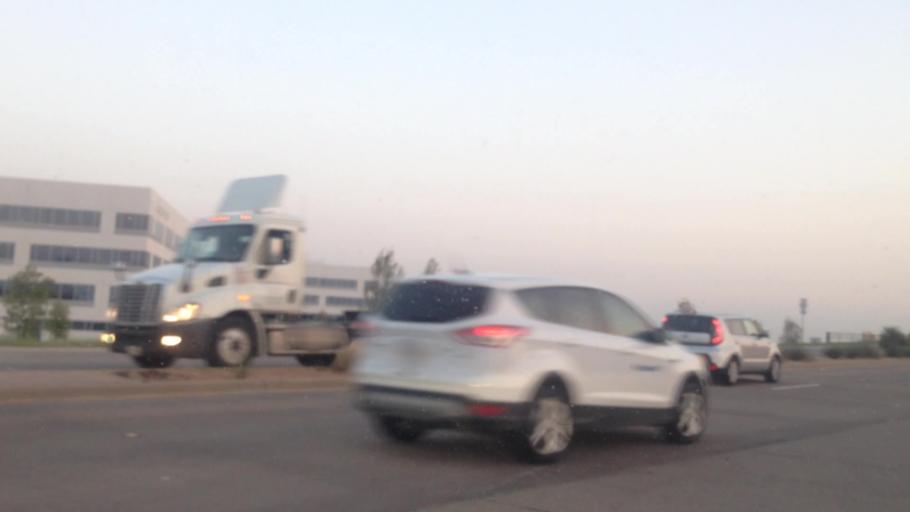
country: US
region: Texas
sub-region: Dallas County
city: Coppell
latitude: 32.9328
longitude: -97.0086
